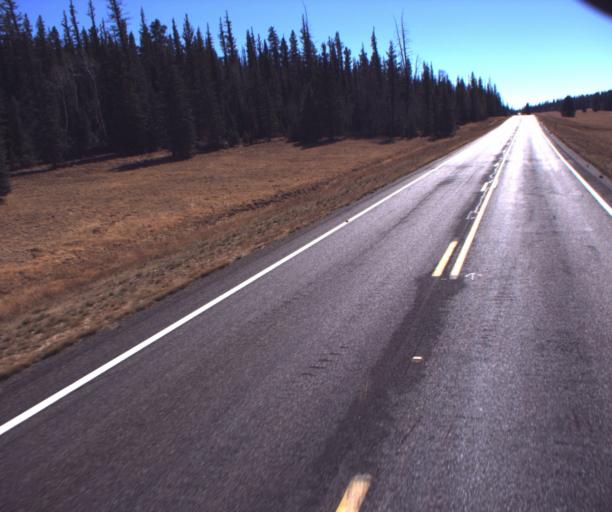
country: US
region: Arizona
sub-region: Coconino County
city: Grand Canyon
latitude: 36.3535
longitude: -112.1183
